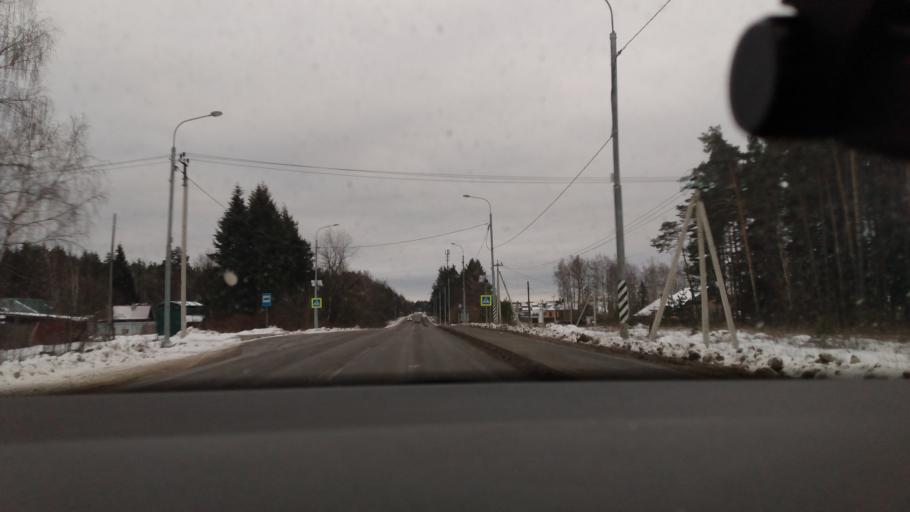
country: RU
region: Moskovskaya
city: Yegor'yevsk
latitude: 55.3536
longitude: 39.0735
